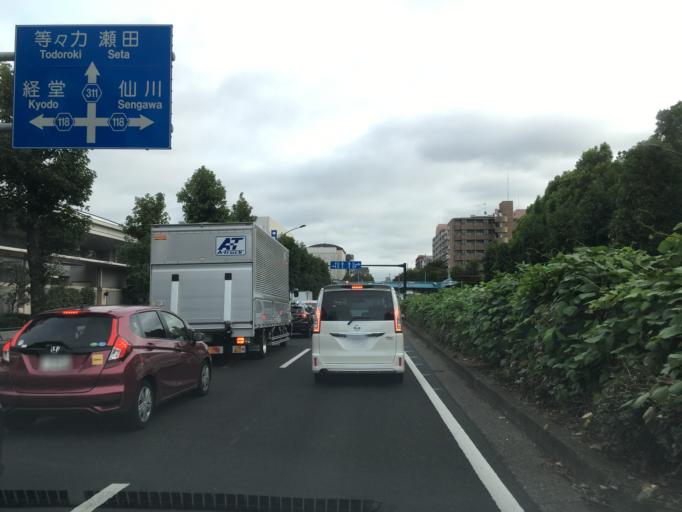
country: JP
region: Tokyo
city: Mitaka-shi
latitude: 35.6607
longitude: 139.6146
